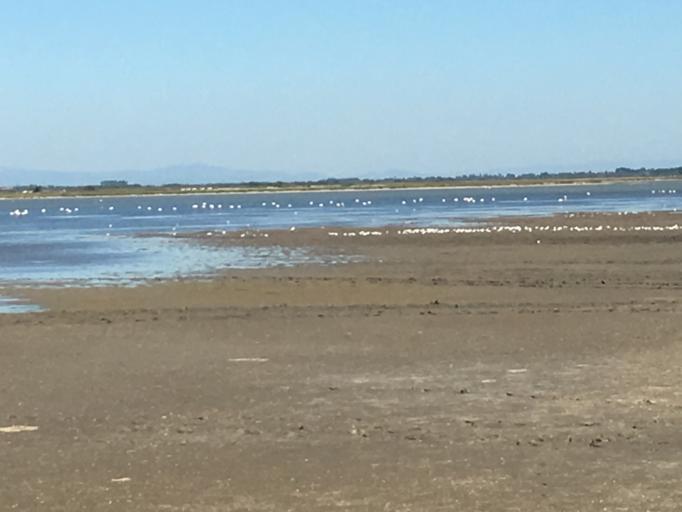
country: FR
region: Provence-Alpes-Cote d'Azur
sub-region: Departement des Bouches-du-Rhone
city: Saintes-Maries-de-la-Mer
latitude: 43.4624
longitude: 4.4561
